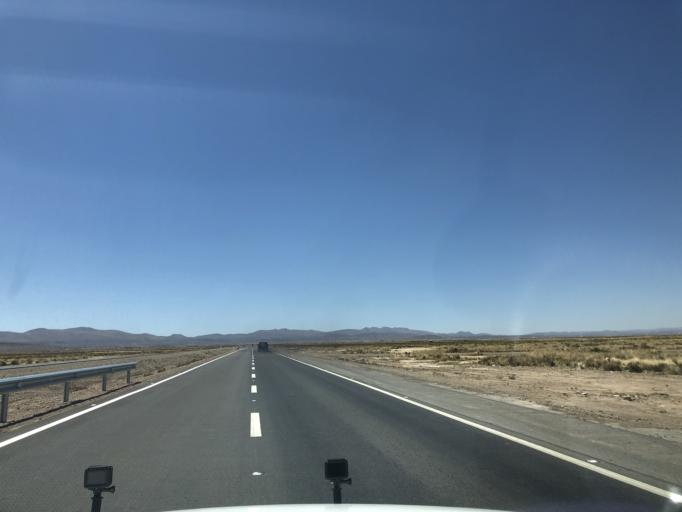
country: BO
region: La Paz
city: Colquiri
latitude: -17.6496
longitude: -67.1962
